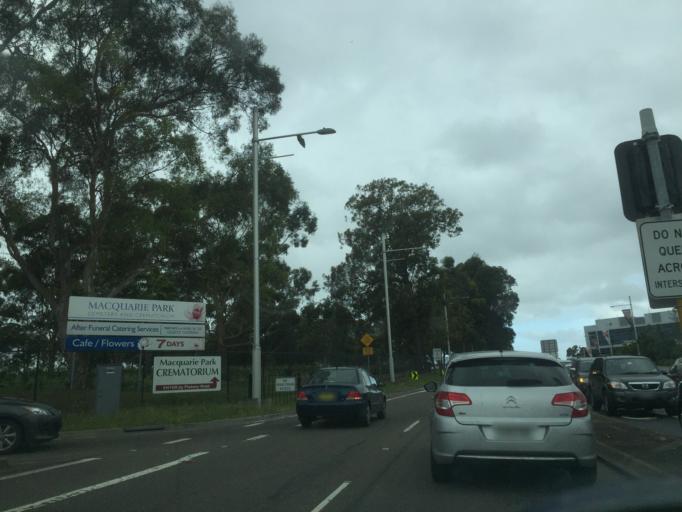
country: AU
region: New South Wales
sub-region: Ryde
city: North Ryde
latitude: -33.7939
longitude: 151.1362
